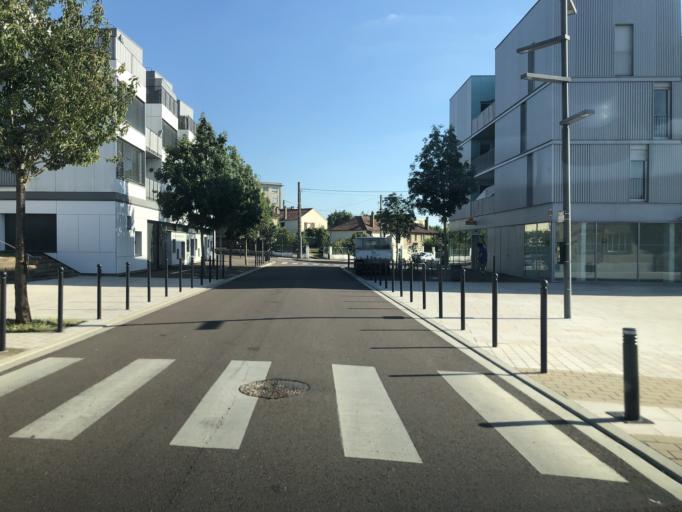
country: FR
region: Bourgogne
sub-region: Departement de l'Yonne
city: Auxerre
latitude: 47.7952
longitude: 3.5888
